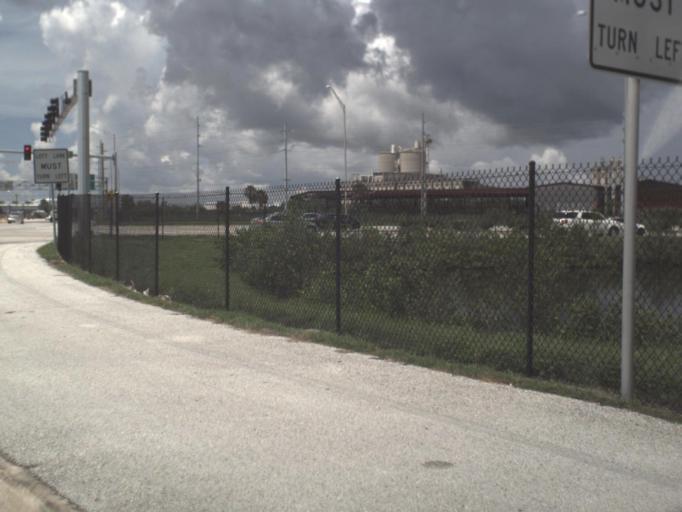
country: US
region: Florida
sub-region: Hillsborough County
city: Tampa
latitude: 27.9374
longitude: -82.4349
